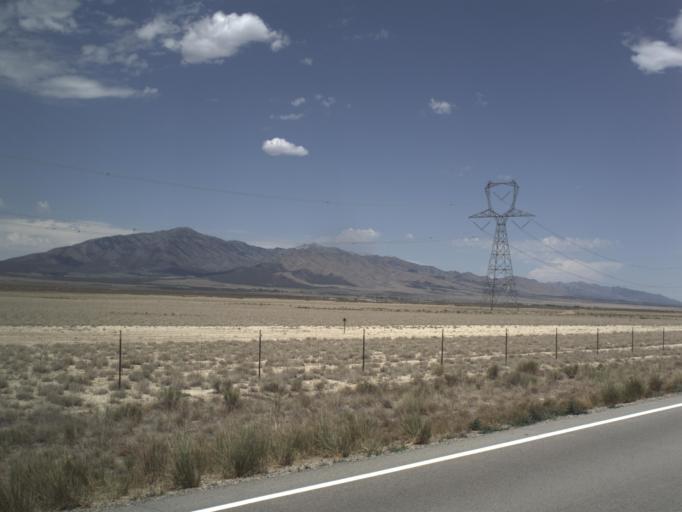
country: US
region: Utah
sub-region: Tooele County
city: Tooele
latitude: 40.2734
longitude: -112.3978
